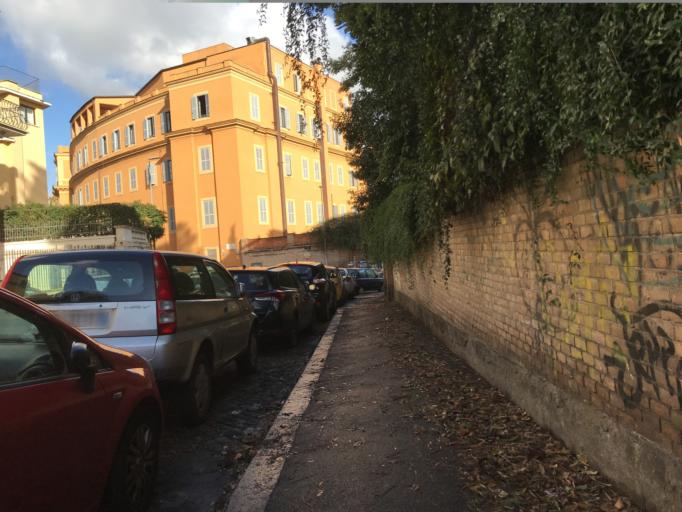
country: IT
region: Latium
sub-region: Citta metropolitana di Roma Capitale
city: Rome
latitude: 41.9111
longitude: 12.5064
